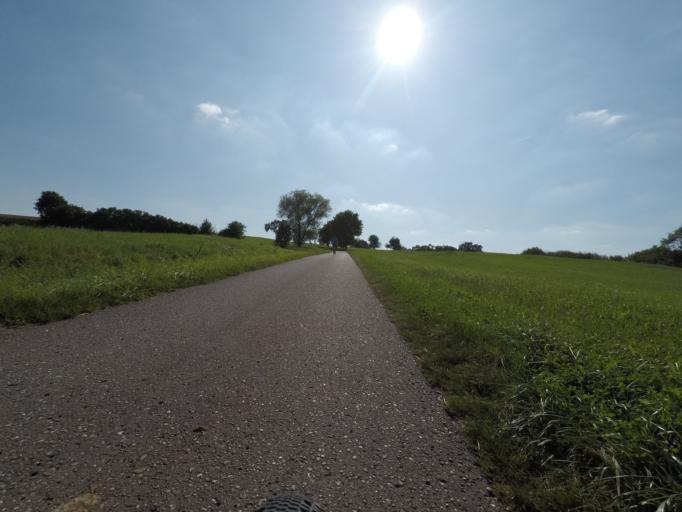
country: DE
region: Baden-Wuerttemberg
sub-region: Regierungsbezirk Stuttgart
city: Hildrizhausen
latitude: 48.6331
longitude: 8.9746
